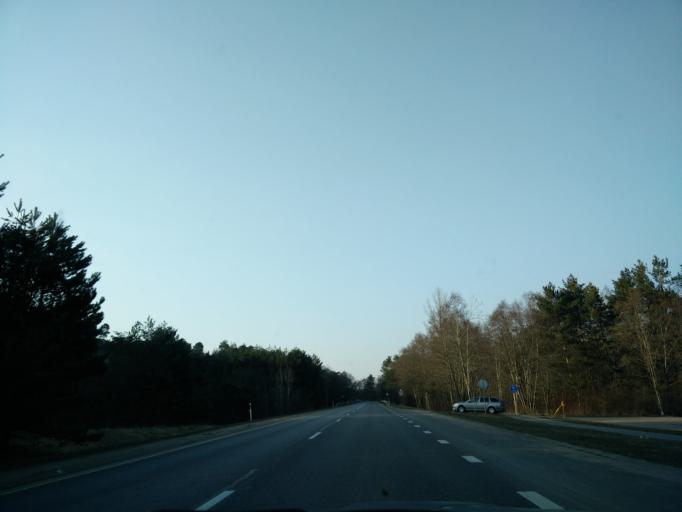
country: LT
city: Trakai
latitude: 54.6584
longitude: 24.9158
